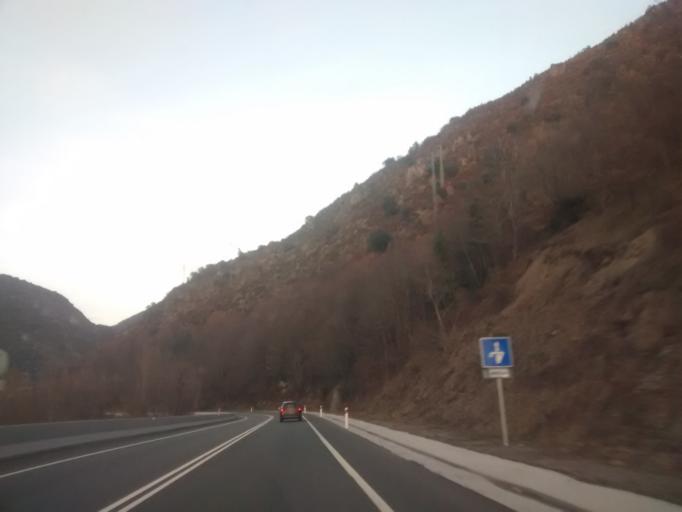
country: ES
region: Catalonia
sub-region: Provincia de Lleida
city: la Seu d'Urgell
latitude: 42.3893
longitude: 1.4615
